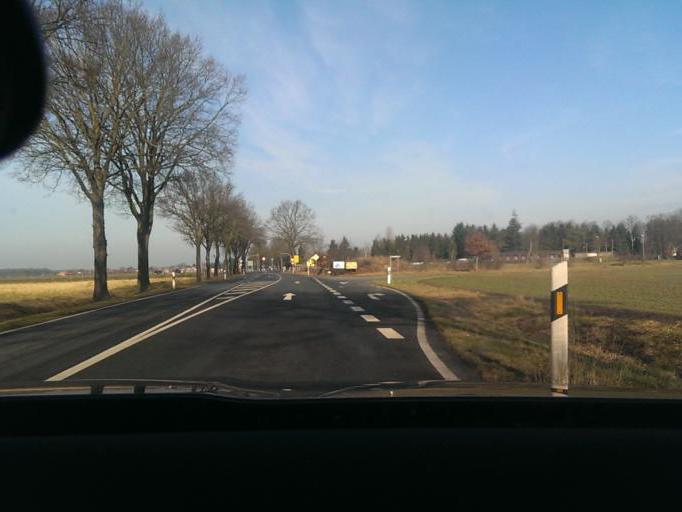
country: DE
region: Lower Saxony
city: Essel
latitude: 52.6783
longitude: 9.6521
